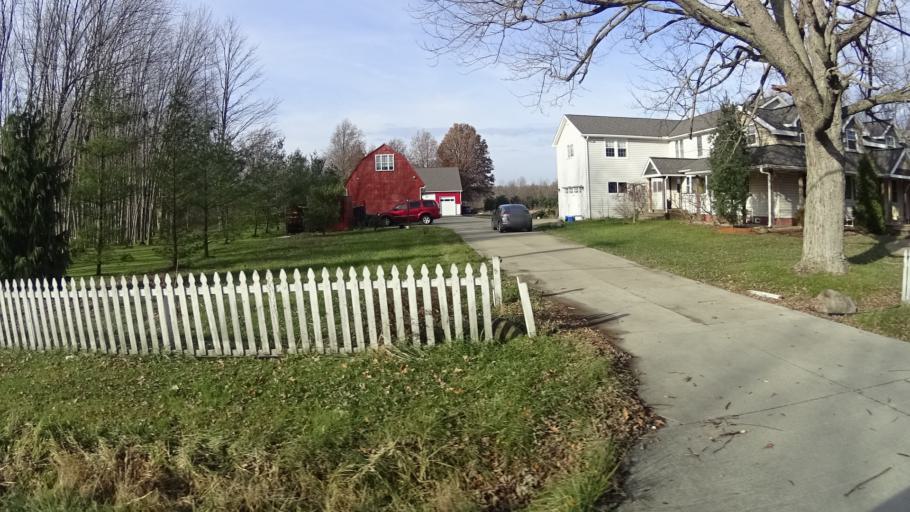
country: US
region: Ohio
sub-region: Lorain County
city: Eaton Estates
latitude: 41.2693
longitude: -81.9825
